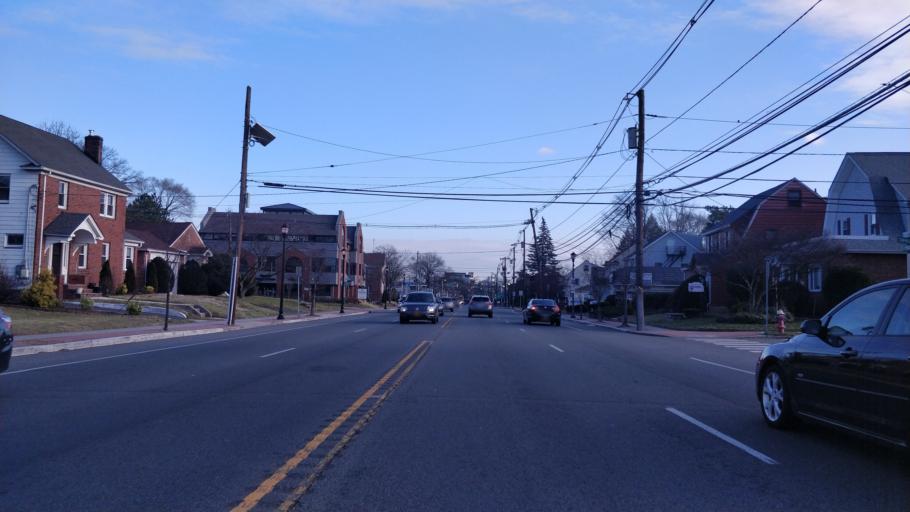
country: US
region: New Jersey
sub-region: Union County
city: Hillside
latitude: 40.6882
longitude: -74.2445
